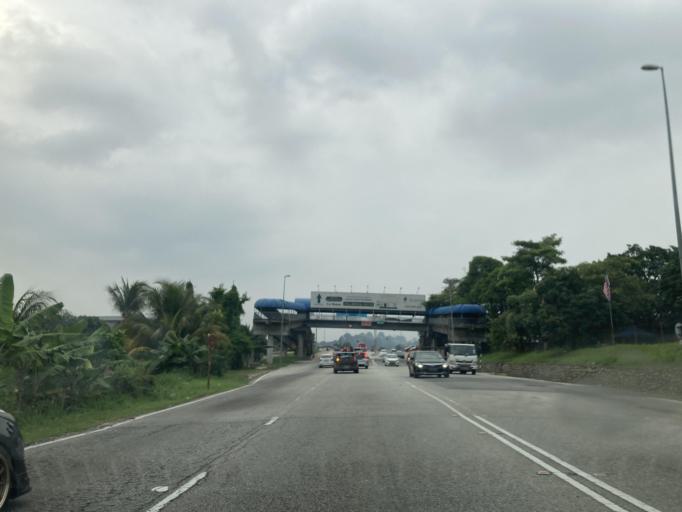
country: MY
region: Selangor
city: Kuang
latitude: 3.2065
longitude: 101.5413
